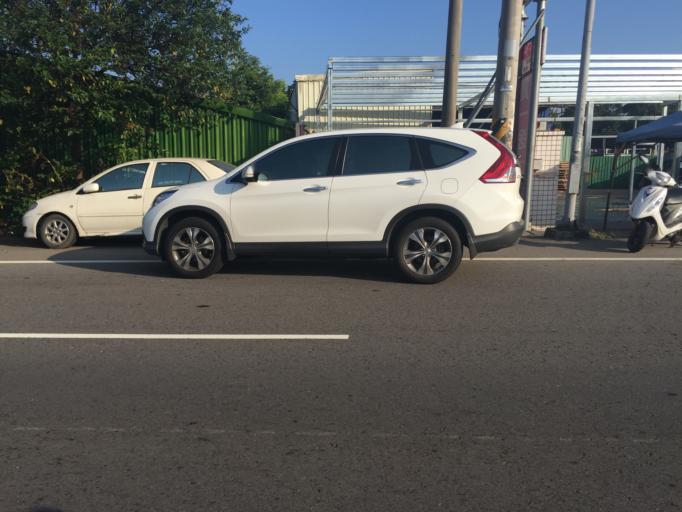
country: TW
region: Taiwan
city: Daxi
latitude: 24.9201
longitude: 121.2550
